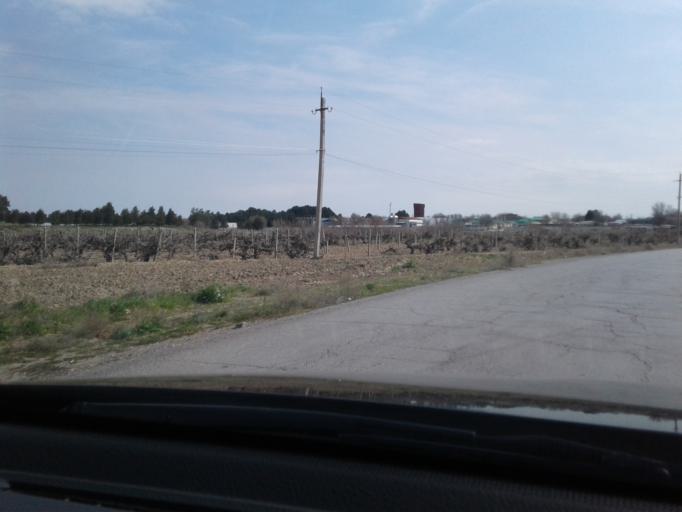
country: TM
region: Ahal
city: Abadan
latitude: 38.1232
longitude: 58.3412
